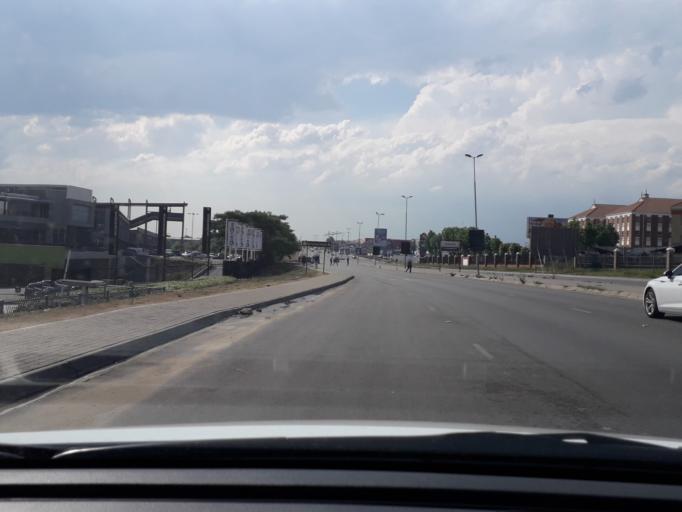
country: ZA
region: Gauteng
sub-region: City of Johannesburg Metropolitan Municipality
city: Diepsloot
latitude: -26.0181
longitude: 28.0017
